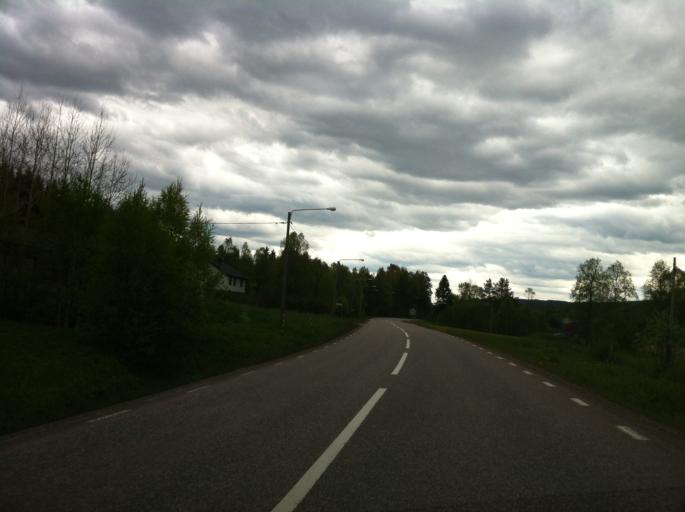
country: SE
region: Dalarna
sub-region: Malung-Saelens kommun
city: Malung
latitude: 61.1340
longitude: 13.2825
